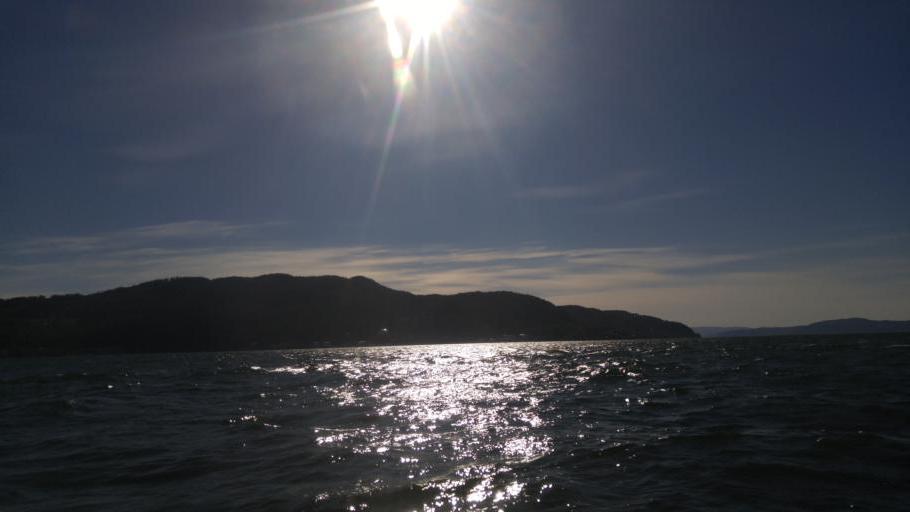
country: NO
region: Sor-Trondelag
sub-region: Trondheim
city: Trondheim
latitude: 63.4430
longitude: 10.3901
